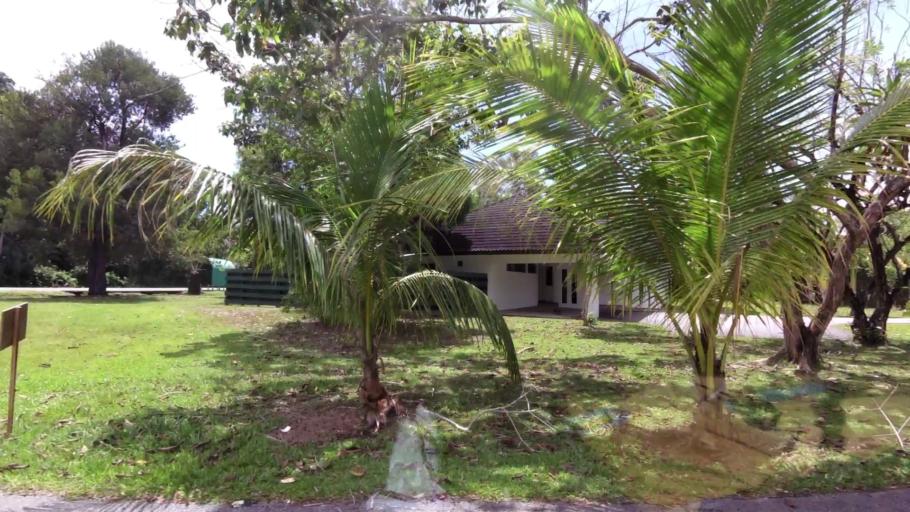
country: BN
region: Belait
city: Kuala Belait
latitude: 4.5966
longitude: 114.2573
